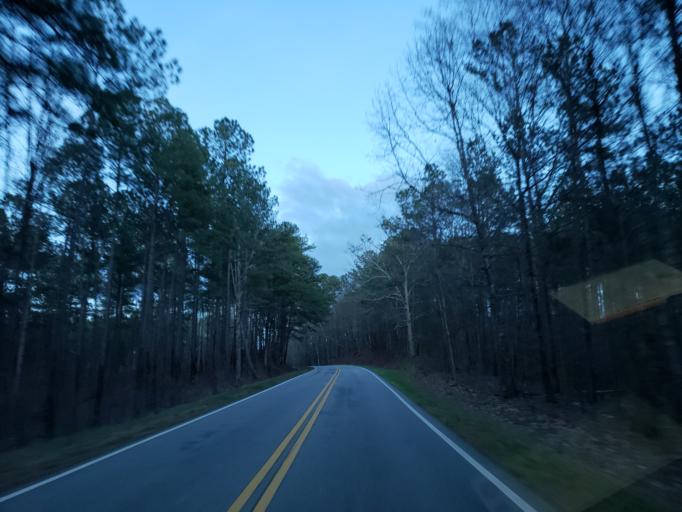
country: US
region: Georgia
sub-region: Polk County
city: Rockmart
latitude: 33.9890
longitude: -84.9398
